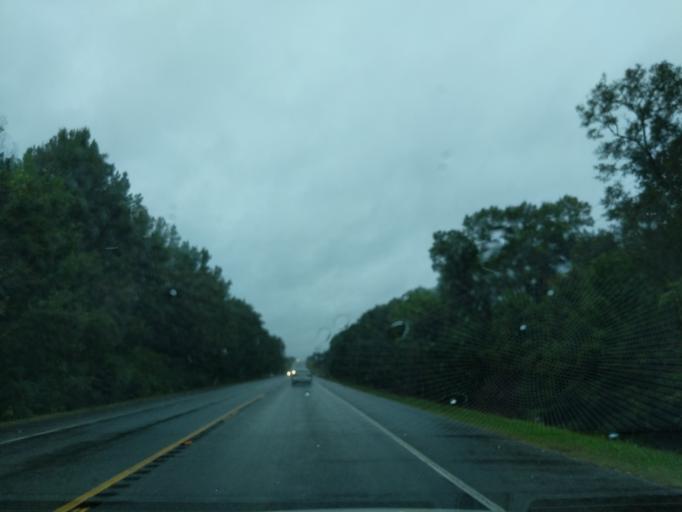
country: US
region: Louisiana
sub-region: Webster Parish
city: Minden
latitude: 32.6221
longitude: -93.2497
